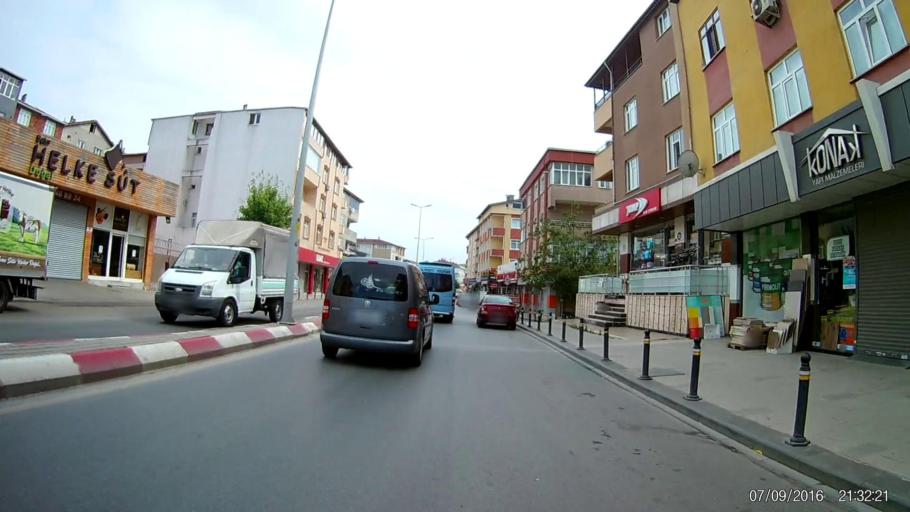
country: TR
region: Istanbul
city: Sultanbeyli
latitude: 40.9803
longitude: 29.2657
